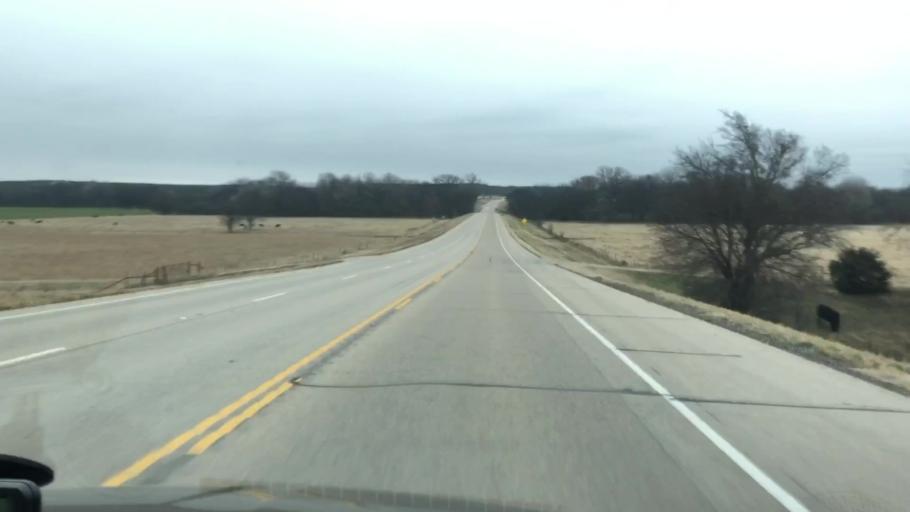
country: US
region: Texas
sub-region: Hamilton County
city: Hamilton
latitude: 31.7835
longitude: -98.1224
